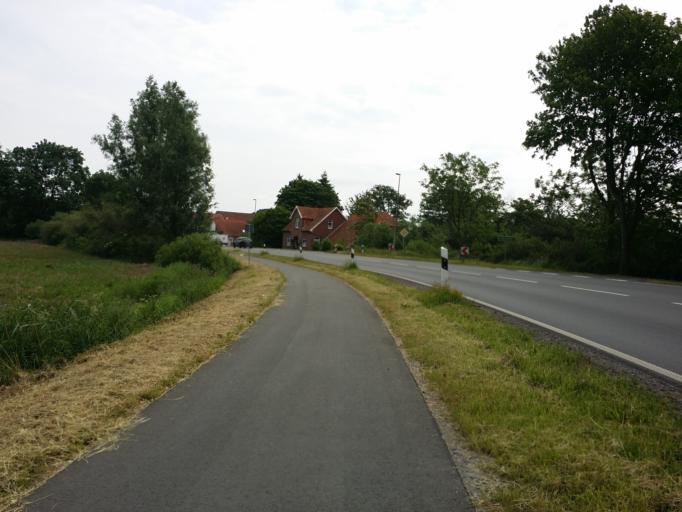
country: DE
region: Lower Saxony
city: Friedeburg
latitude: 53.4485
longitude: 7.8455
